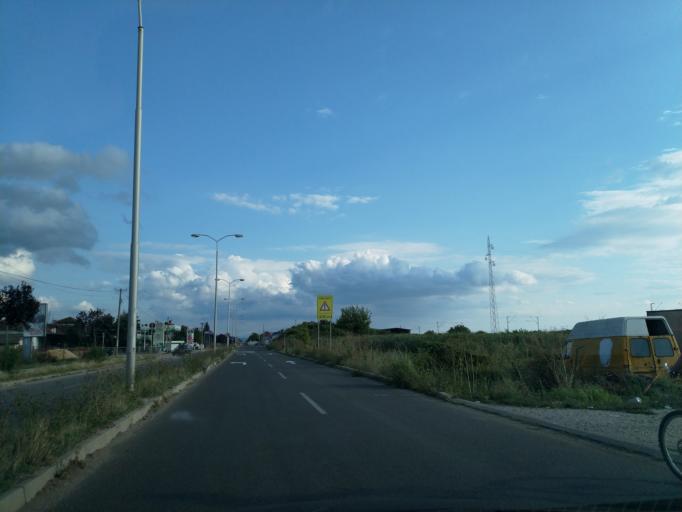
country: RS
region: Central Serbia
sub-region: Pomoravski Okrug
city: Paracin
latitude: 43.8457
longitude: 21.4142
